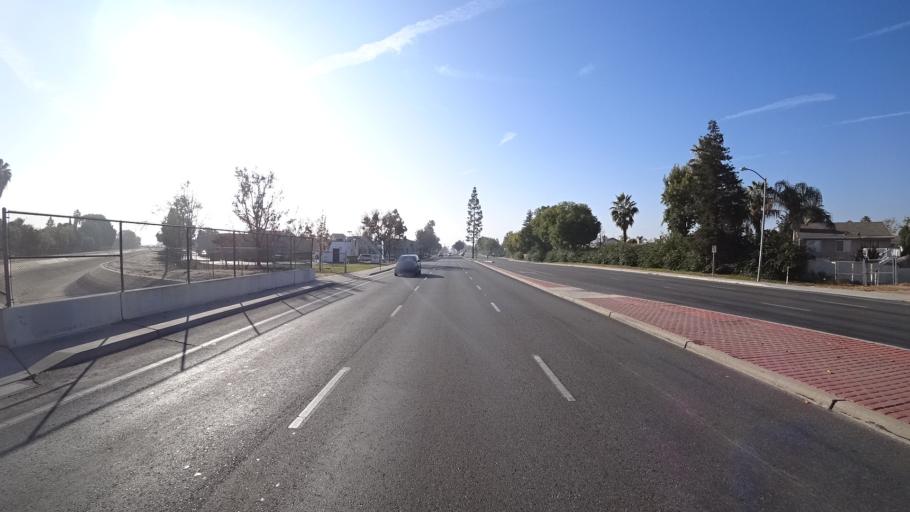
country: US
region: California
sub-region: Kern County
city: Greenacres
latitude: 35.3217
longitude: -119.0921
